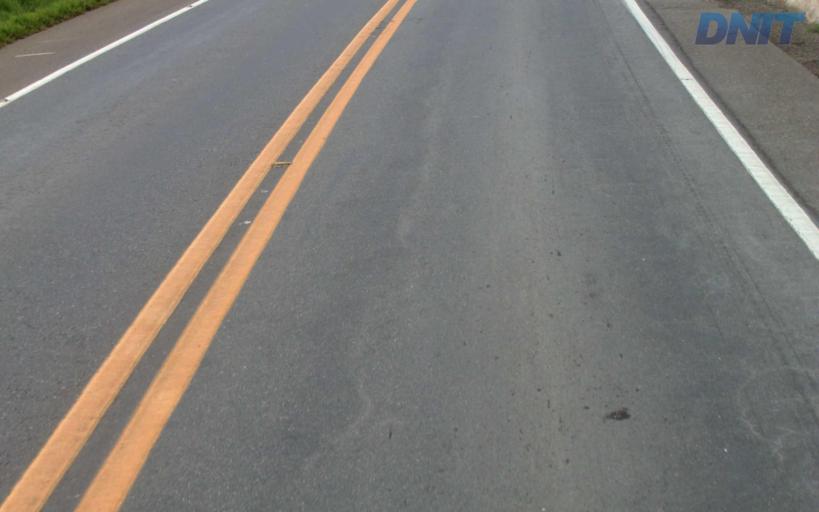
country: BR
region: Minas Gerais
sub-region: Governador Valadares
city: Governador Valadares
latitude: -18.9658
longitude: -42.0868
